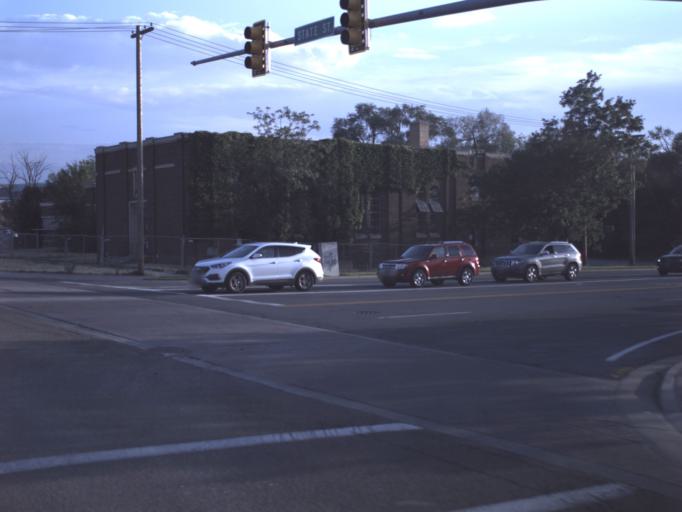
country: US
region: Utah
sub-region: Salt Lake County
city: White City
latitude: 40.5518
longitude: -111.8909
